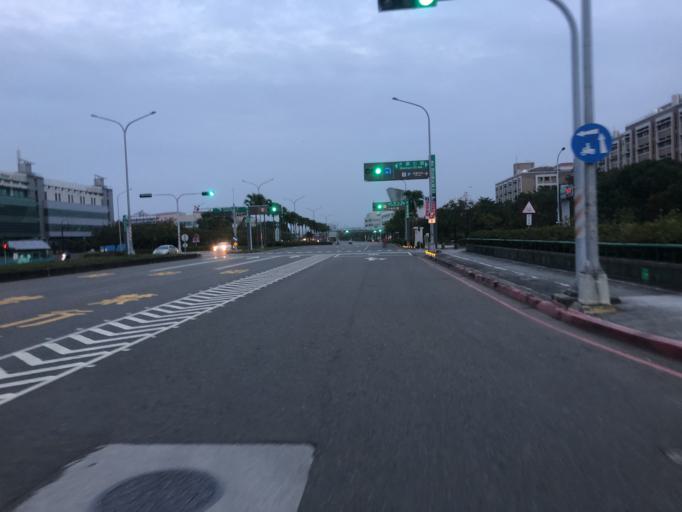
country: TW
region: Taiwan
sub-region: Tainan
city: Tainan
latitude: 23.1034
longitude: 120.2864
